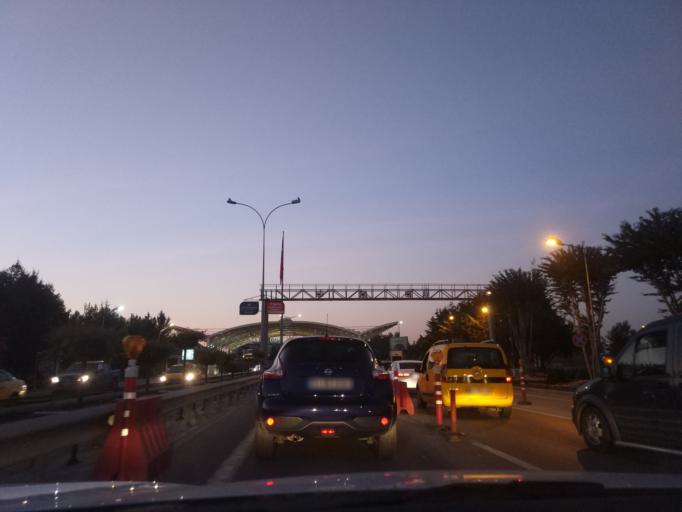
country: TR
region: Istanbul
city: Pendik
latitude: 40.9128
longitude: 29.3131
